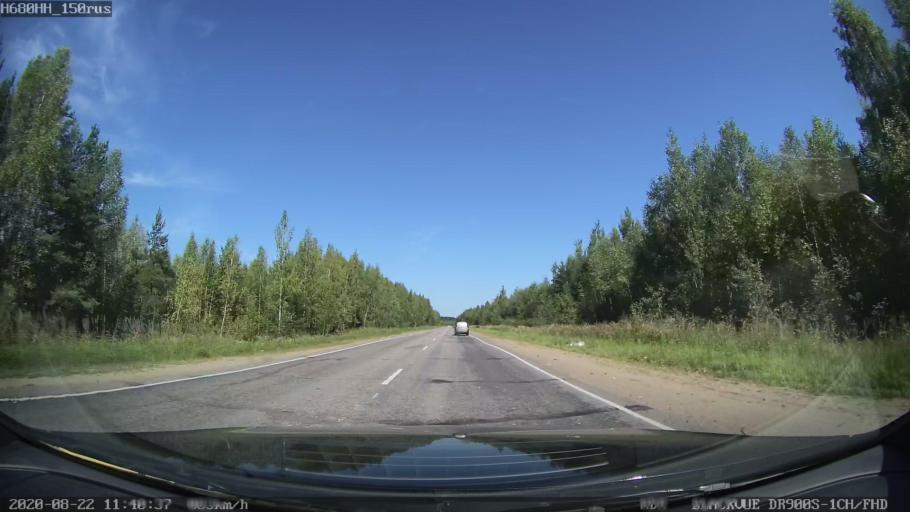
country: RU
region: Tverskaya
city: Sakharovo
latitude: 56.9791
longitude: 36.0235
